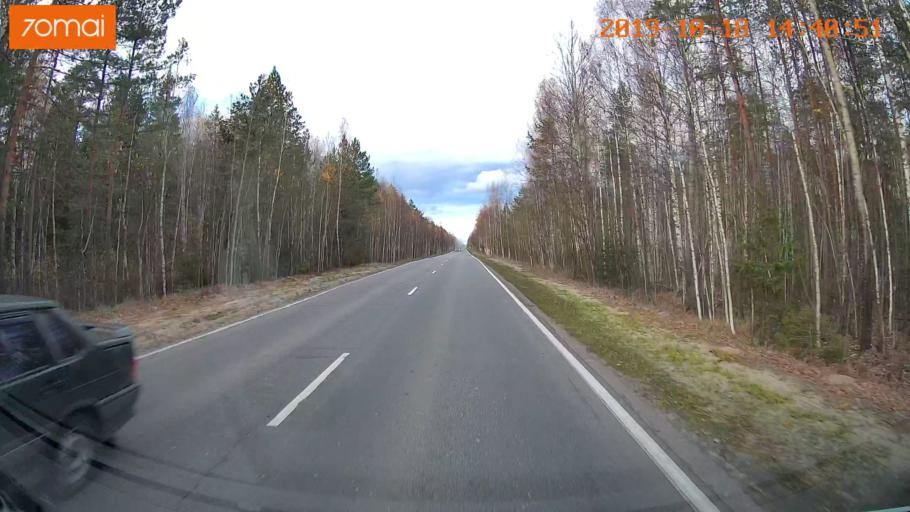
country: RU
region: Vladimir
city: Velikodvorskiy
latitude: 55.2829
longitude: 40.6698
